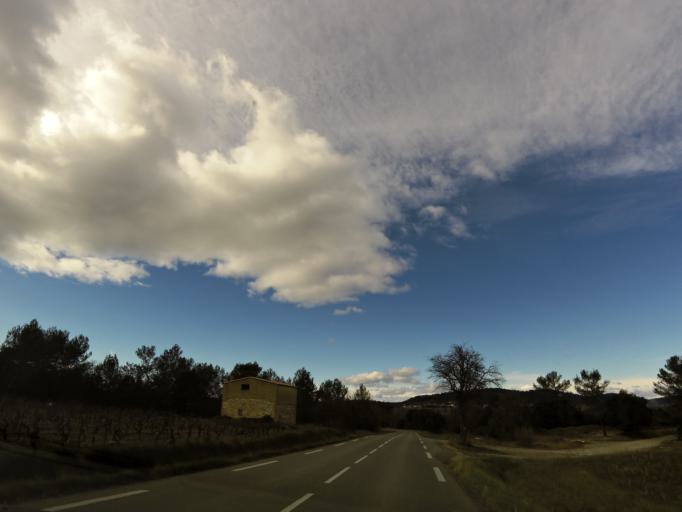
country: FR
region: Languedoc-Roussillon
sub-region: Departement du Gard
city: Sommieres
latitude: 43.8264
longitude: 4.0482
